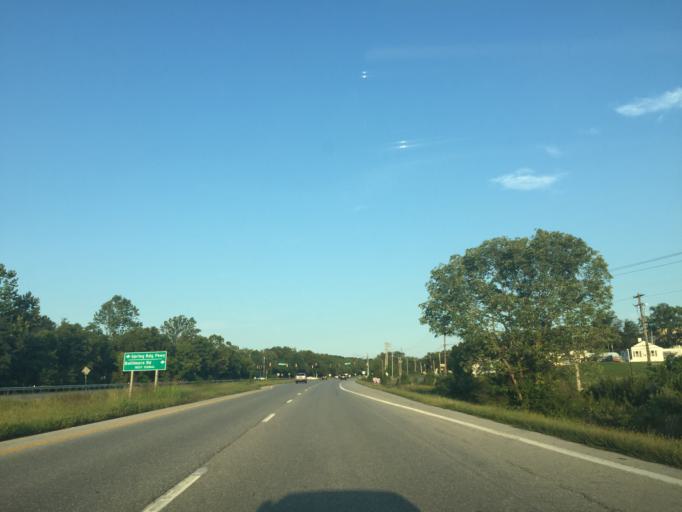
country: US
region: Maryland
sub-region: Frederick County
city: Spring Ridge
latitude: 39.3968
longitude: -77.3525
